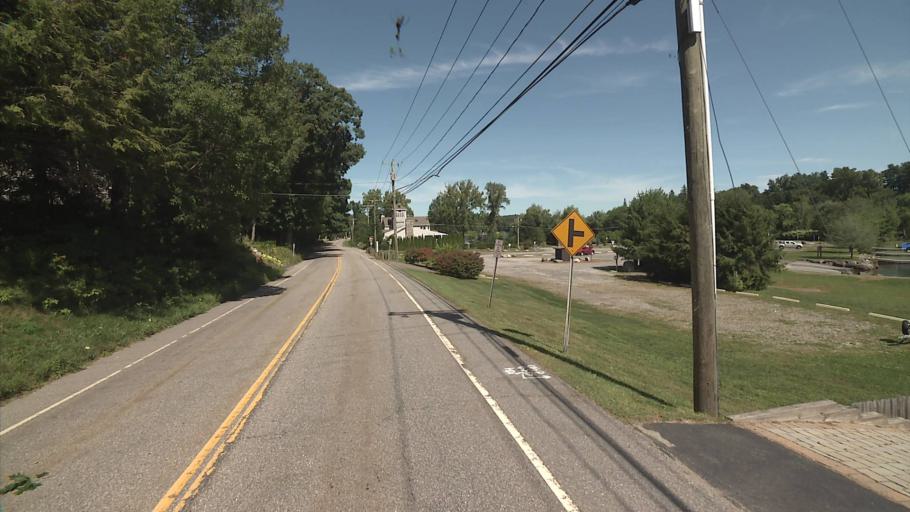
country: US
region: Connecticut
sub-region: Litchfield County
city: Bethlehem Village
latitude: 41.6932
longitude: -73.2319
